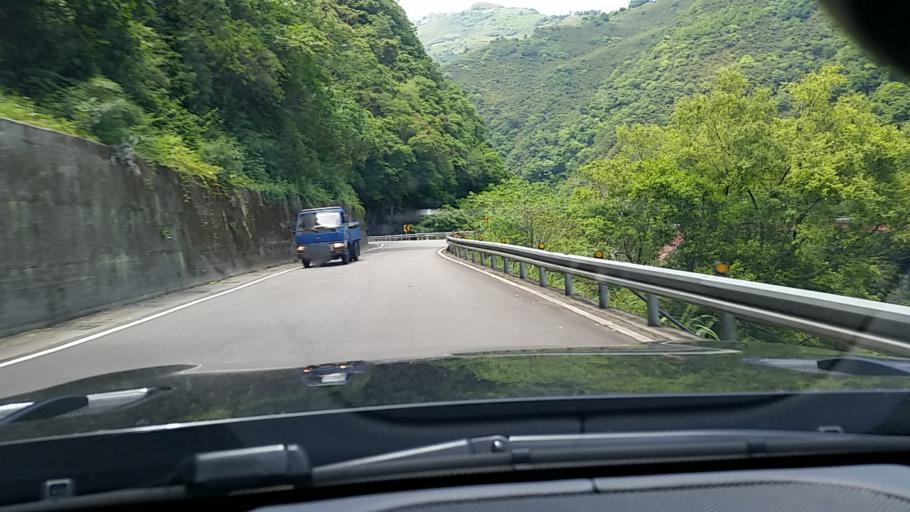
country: TW
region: Taiwan
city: Daxi
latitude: 24.6986
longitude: 121.3628
